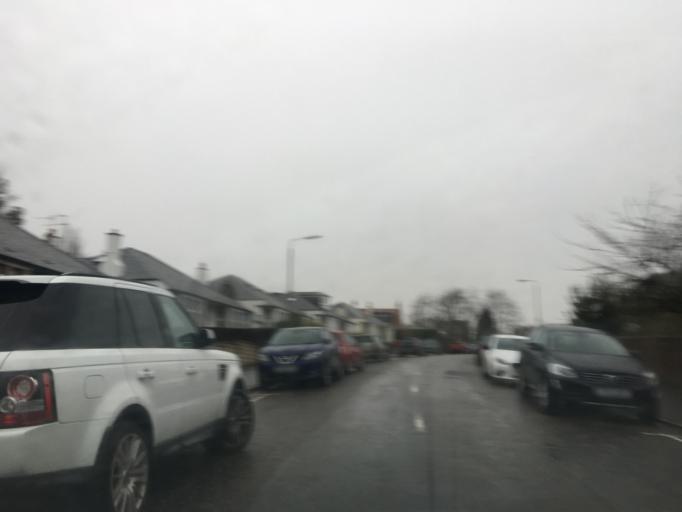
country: GB
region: Scotland
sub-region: Edinburgh
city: Colinton
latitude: 55.9440
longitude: -3.2911
